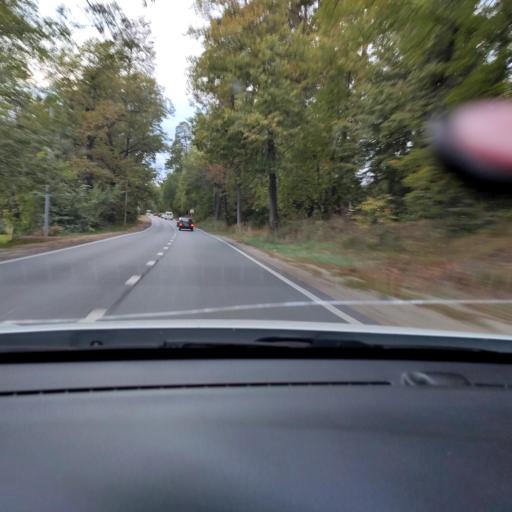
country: RU
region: Mariy-El
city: Volzhsk
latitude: 55.8415
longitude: 48.4293
